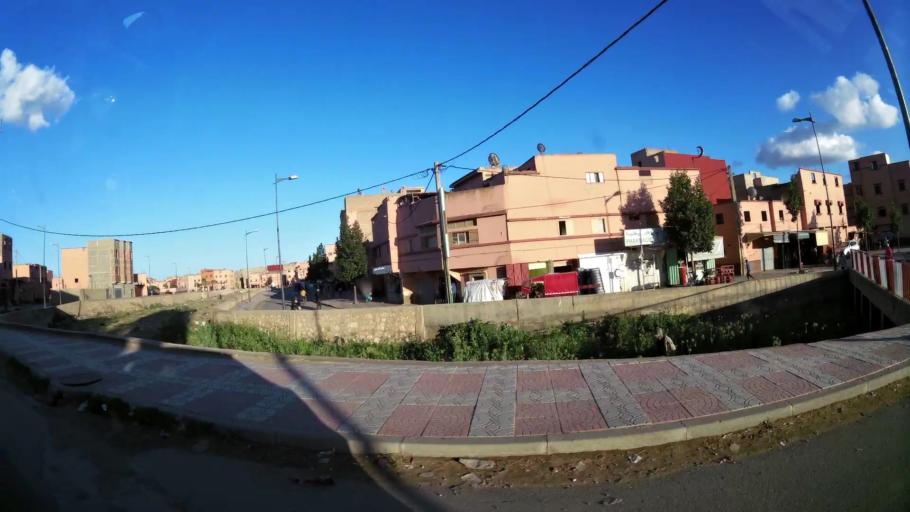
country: MA
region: Marrakech-Tensift-Al Haouz
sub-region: Kelaa-Des-Sraghna
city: Sidi Abdallah
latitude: 32.2453
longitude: -7.9477
